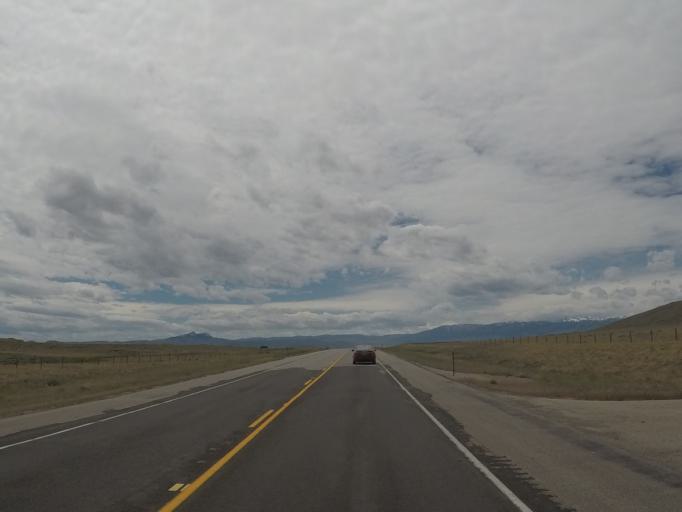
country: US
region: Montana
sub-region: Carbon County
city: Red Lodge
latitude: 44.9460
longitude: -109.0731
